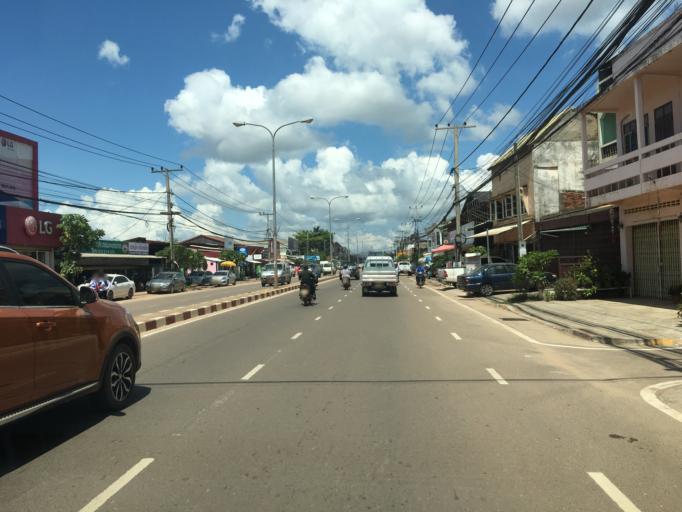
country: TH
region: Nong Khai
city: Si Chiang Mai
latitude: 17.9733
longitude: 102.5624
